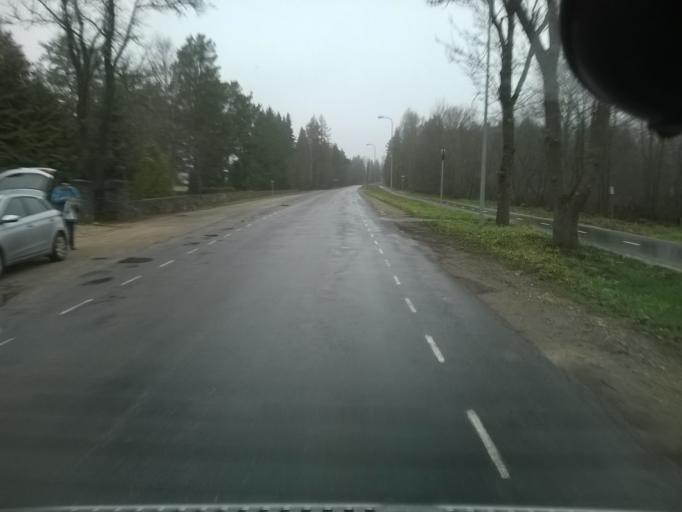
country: EE
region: Raplamaa
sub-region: Kohila vald
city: Kohila
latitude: 59.1663
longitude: 24.6520
